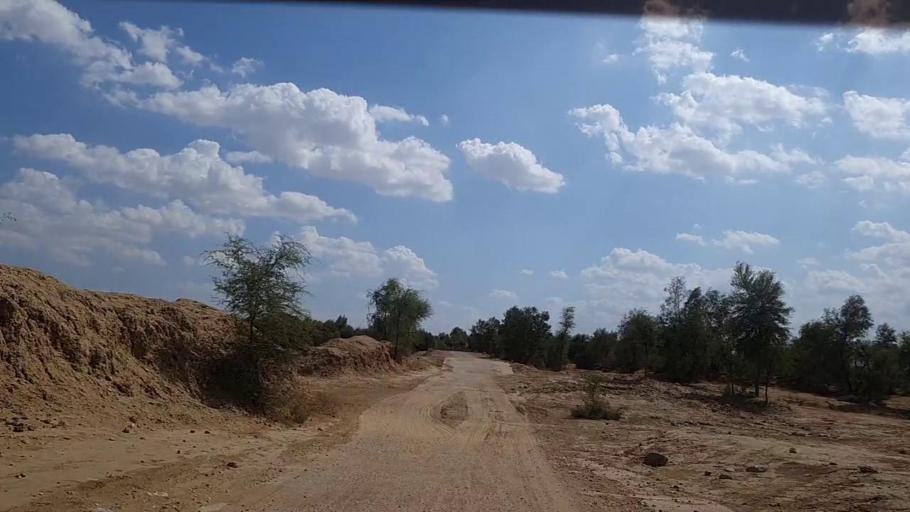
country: PK
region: Sindh
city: Johi
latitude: 26.5193
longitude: 67.4527
